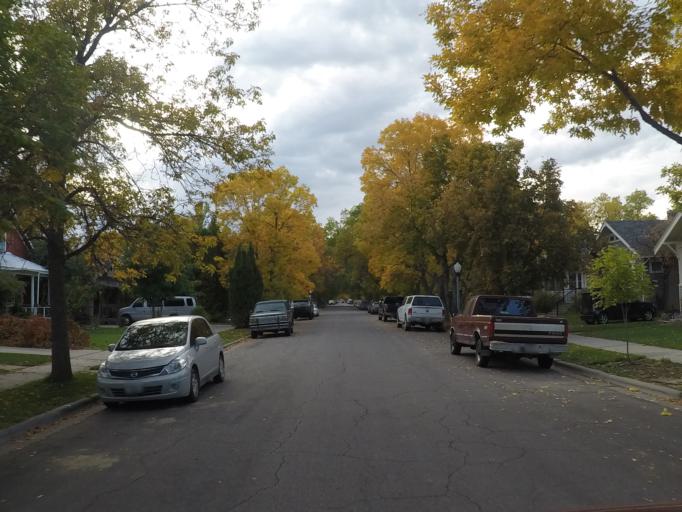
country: US
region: Montana
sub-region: Yellowstone County
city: Billings
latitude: 45.7821
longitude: -108.5167
